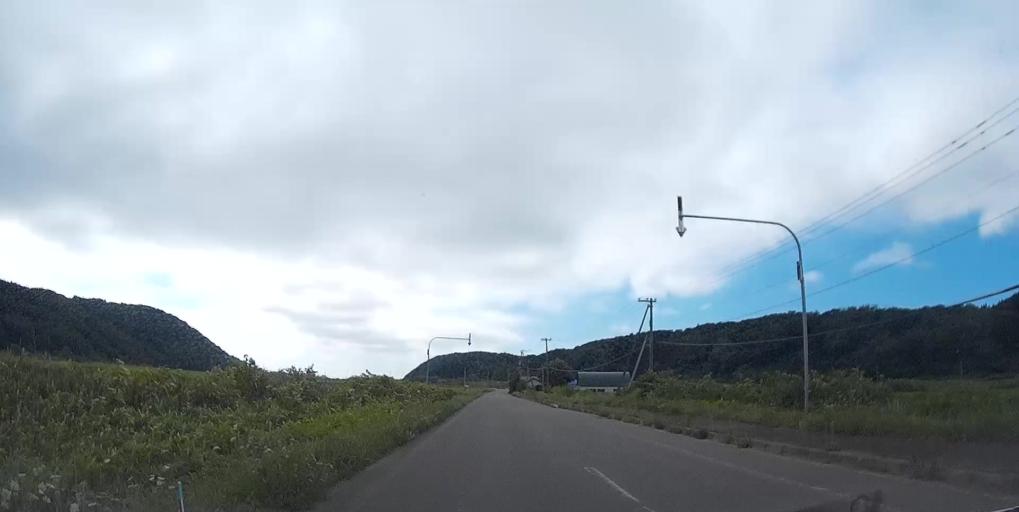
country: JP
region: Hokkaido
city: Kamiiso
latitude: 41.9731
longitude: 140.1633
